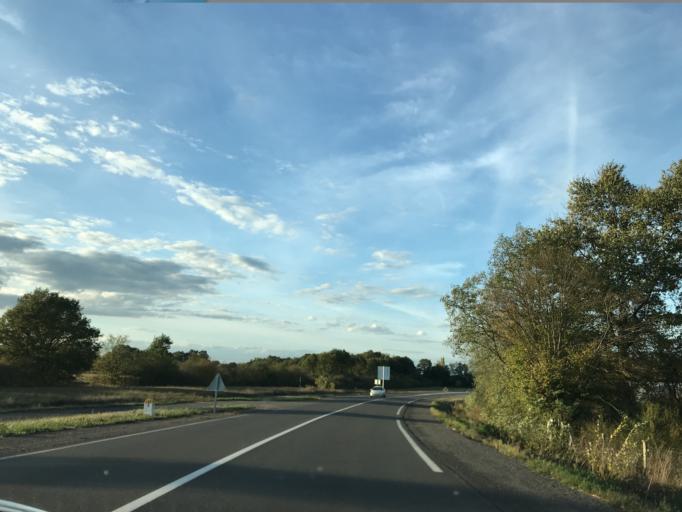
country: FR
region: Auvergne
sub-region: Departement de l'Allier
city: Saint-Yorre
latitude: 46.0468
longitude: 3.4713
